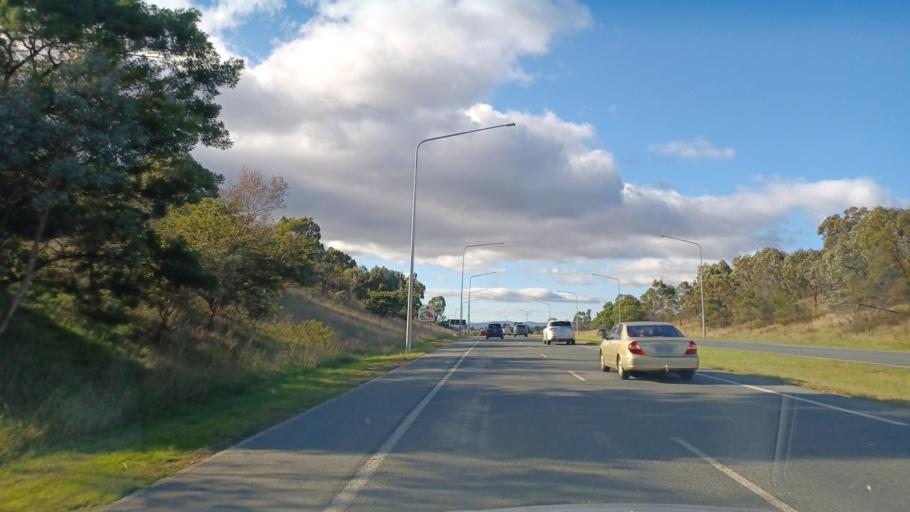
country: AU
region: Australian Capital Territory
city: Macquarie
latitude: -35.2728
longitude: 149.0603
